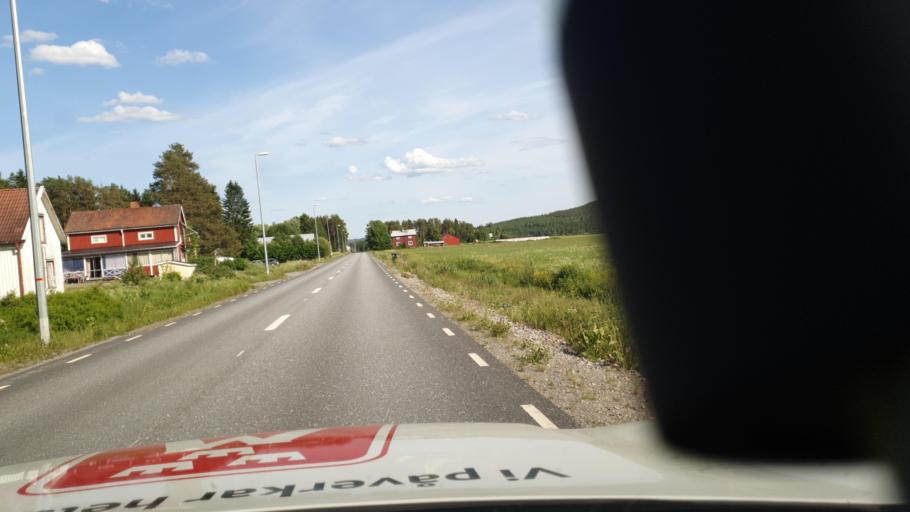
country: SE
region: Vaesterbotten
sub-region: Skelleftea Kommun
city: Forsbacka
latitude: 64.6895
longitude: 20.5094
